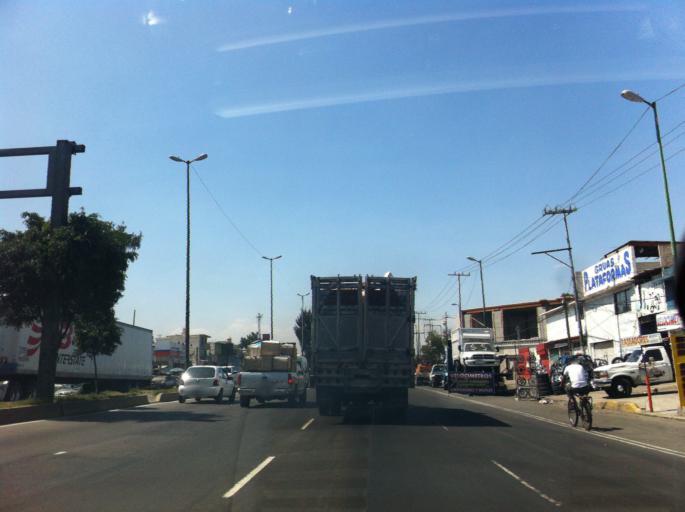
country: MX
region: Mexico
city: Los Reyes La Paz
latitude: 19.3558
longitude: -99.0071
